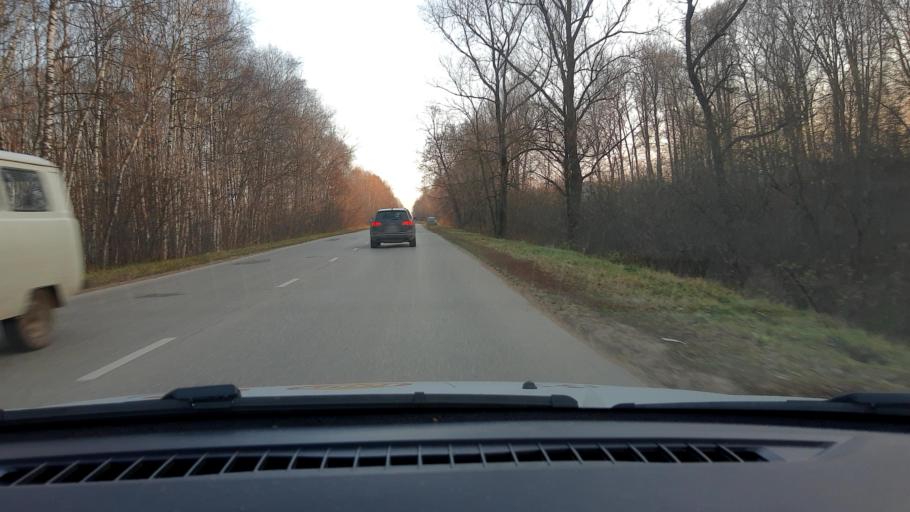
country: RU
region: Nizjnij Novgorod
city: Volodarsk
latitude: 56.2522
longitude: 43.1733
